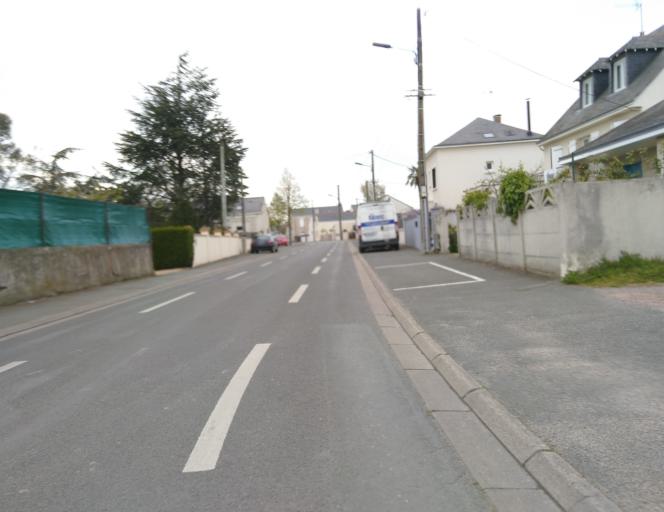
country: FR
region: Pays de la Loire
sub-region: Departement de Maine-et-Loire
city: Les Ponts-de-Ce
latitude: 47.4488
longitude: -0.5210
